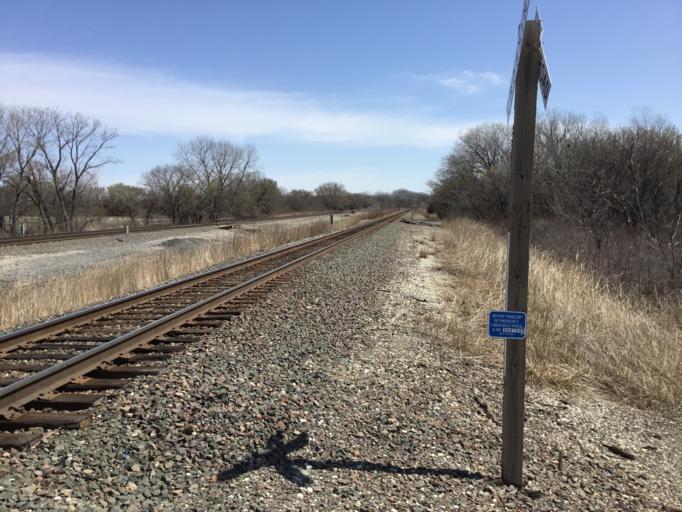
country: US
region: Kansas
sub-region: Lyon County
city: Emporia
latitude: 38.4031
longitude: -96.2812
